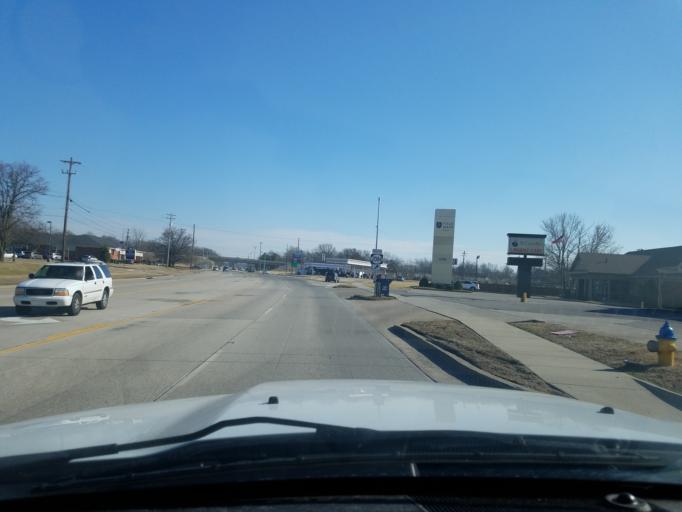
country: US
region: Kentucky
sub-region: Henderson County
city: Henderson
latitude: 37.8317
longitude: -87.5702
